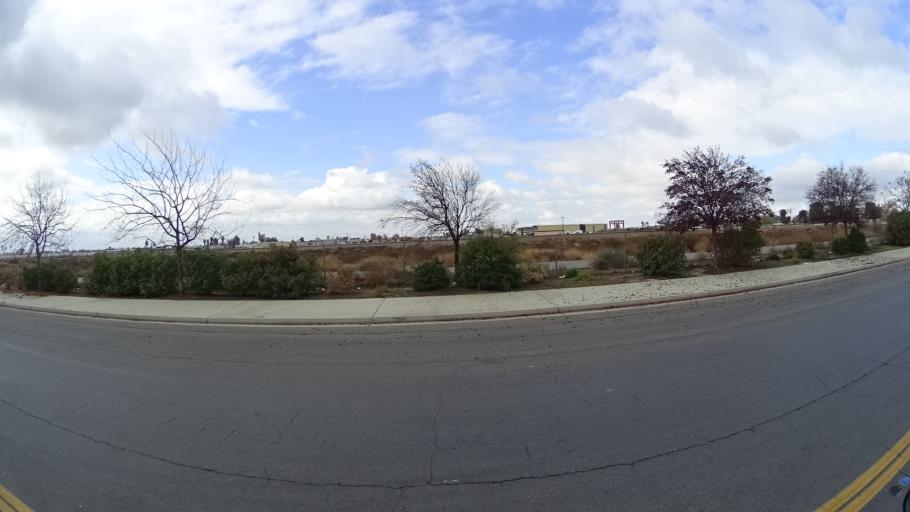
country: US
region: California
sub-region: Kern County
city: Bakersfield
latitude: 35.3347
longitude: -118.9943
